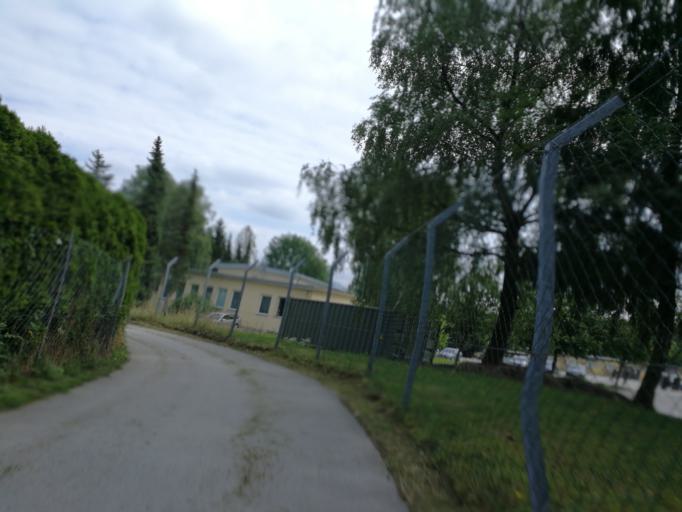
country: DE
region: Bavaria
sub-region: Upper Bavaria
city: Ainring
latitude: 47.8002
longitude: 12.9782
